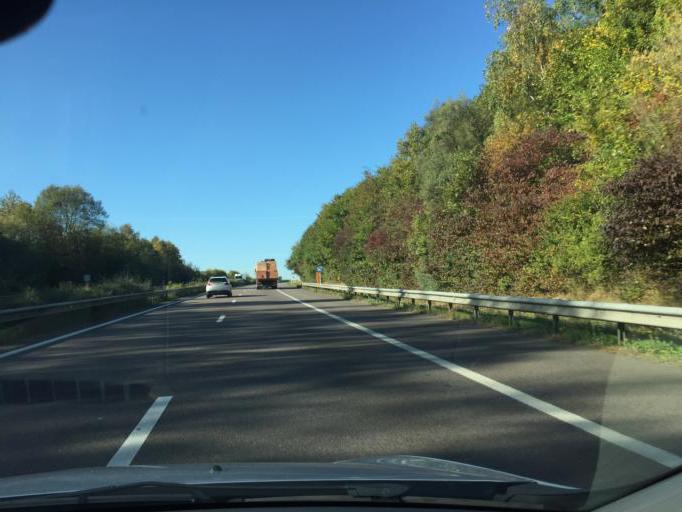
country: LU
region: Grevenmacher
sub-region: Canton de Grevenmacher
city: Betzdorf
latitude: 49.6673
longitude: 6.3751
